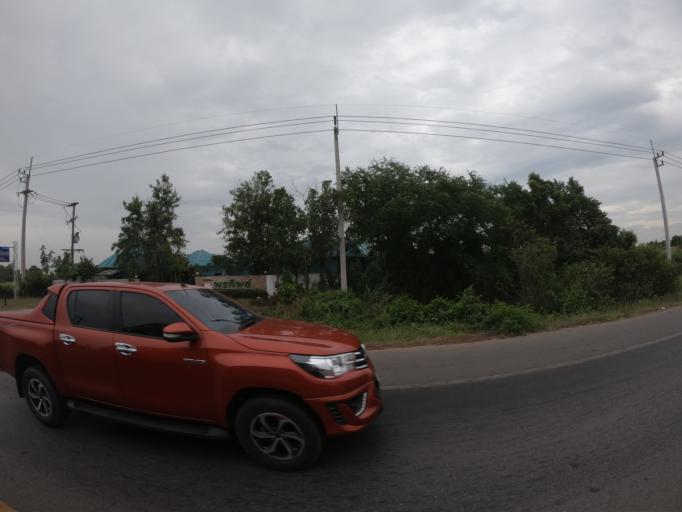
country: TH
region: Roi Et
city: Chiang Khwan
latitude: 16.1082
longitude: 103.8270
